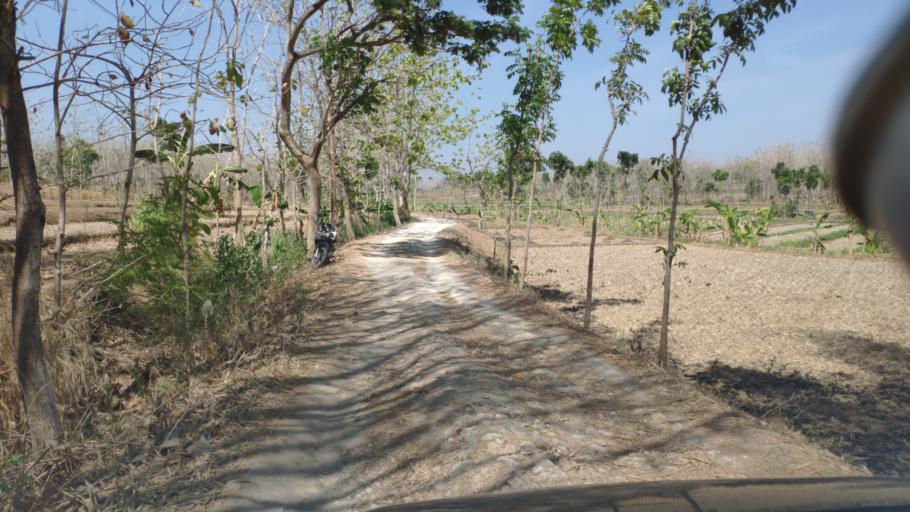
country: ID
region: Central Java
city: Bacem
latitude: -7.0381
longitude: 111.3570
